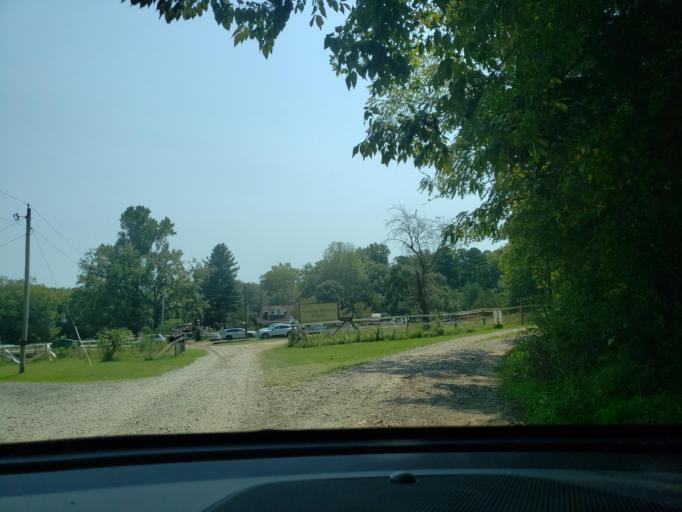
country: US
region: North Carolina
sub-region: Orange County
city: Hillsborough
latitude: 36.0048
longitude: -79.0846
